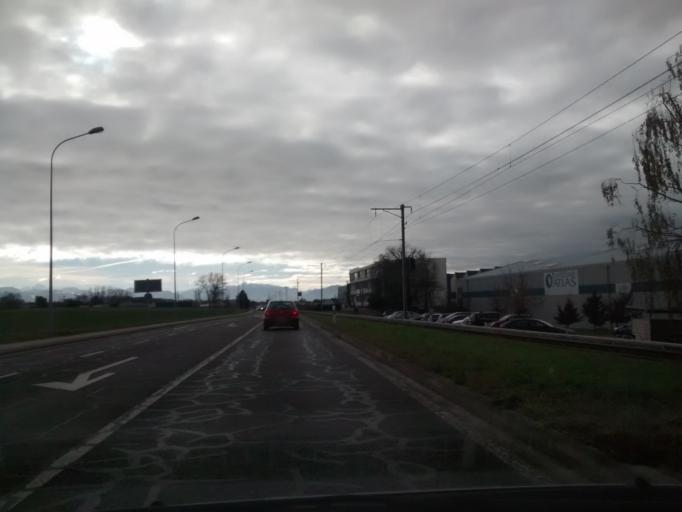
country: CH
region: Vaud
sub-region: Lausanne District
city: Cheseaux
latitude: 46.5777
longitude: 6.6056
